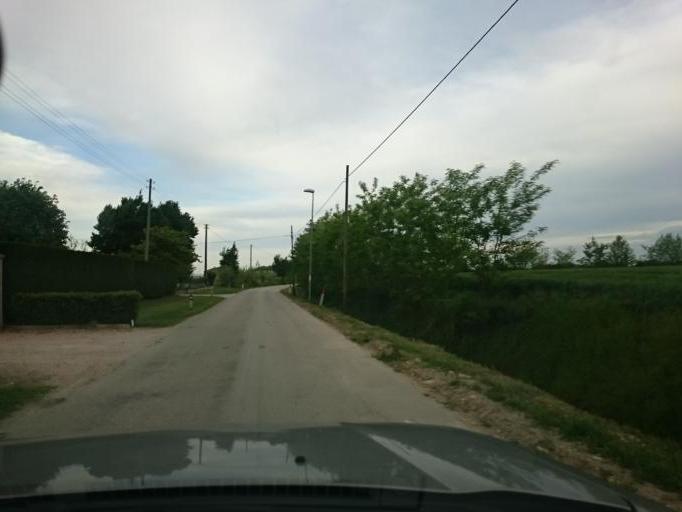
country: IT
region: Veneto
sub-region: Provincia di Padova
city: Cartura
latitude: 45.2840
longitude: 11.8442
